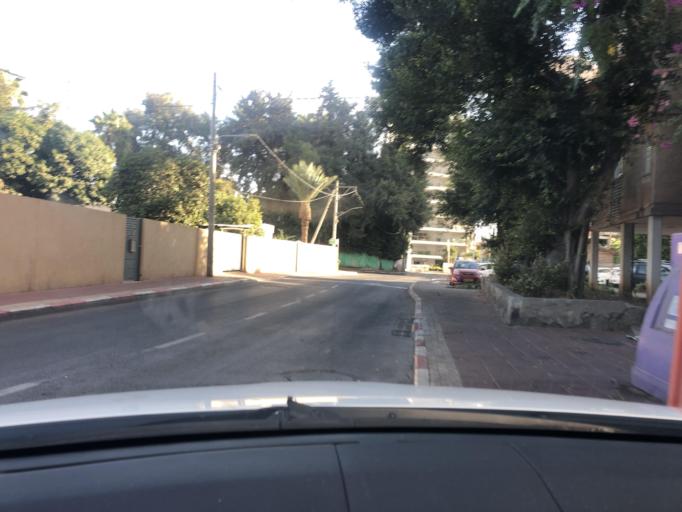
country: IL
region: Tel Aviv
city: Bene Beraq
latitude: 32.0612
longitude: 34.8347
